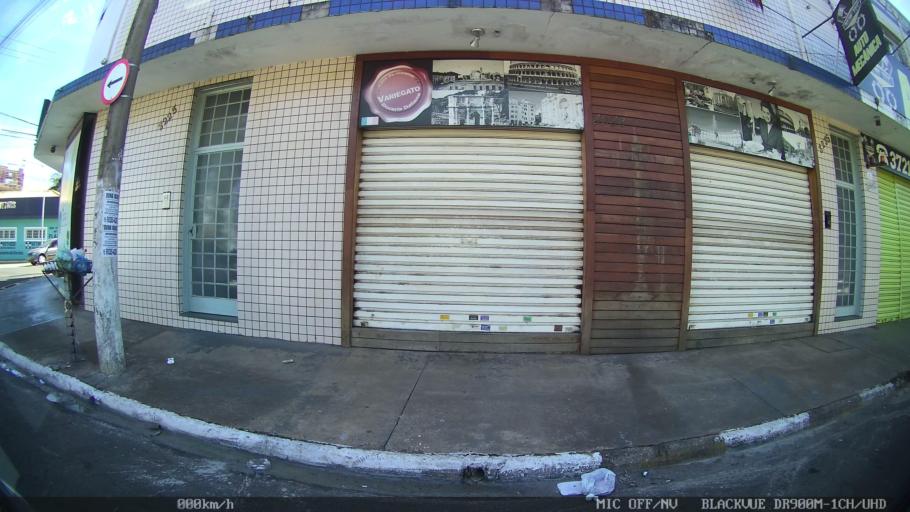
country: BR
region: Sao Paulo
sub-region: Franca
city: Franca
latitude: -20.5366
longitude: -47.3827
